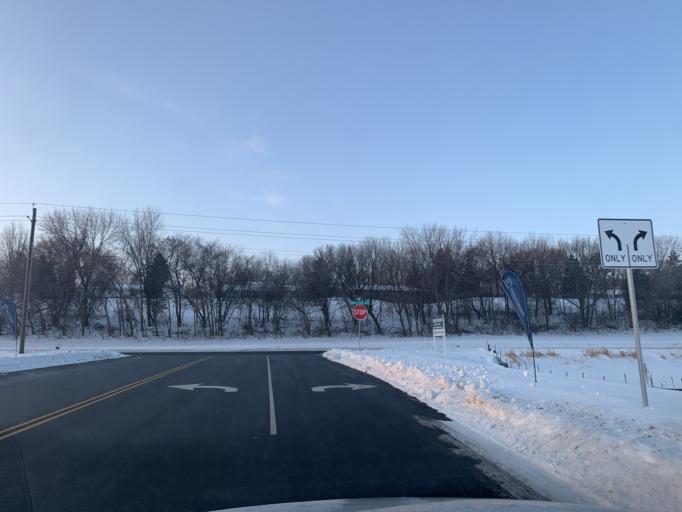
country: US
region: Minnesota
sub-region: Scott County
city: Shakopee
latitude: 44.7856
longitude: -93.4861
